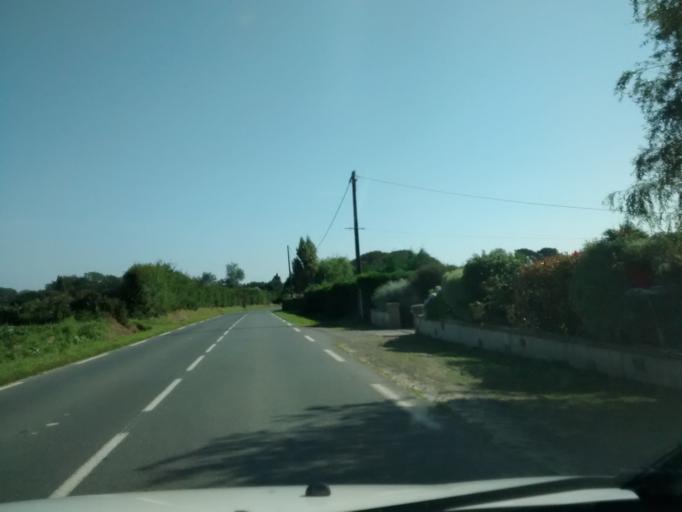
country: FR
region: Brittany
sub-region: Departement des Cotes-d'Armor
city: Pleubian
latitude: 48.8308
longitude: -3.1593
